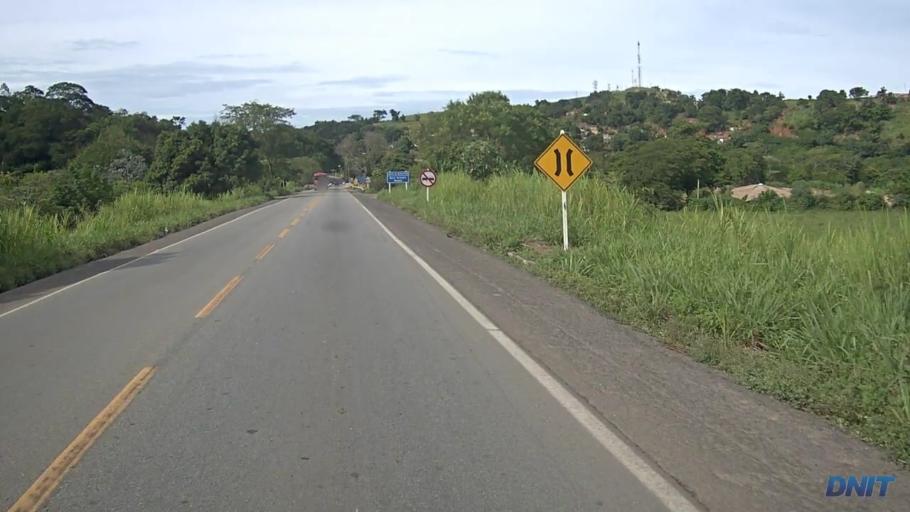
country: BR
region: Minas Gerais
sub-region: Belo Oriente
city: Belo Oriente
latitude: -19.2335
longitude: -42.3292
